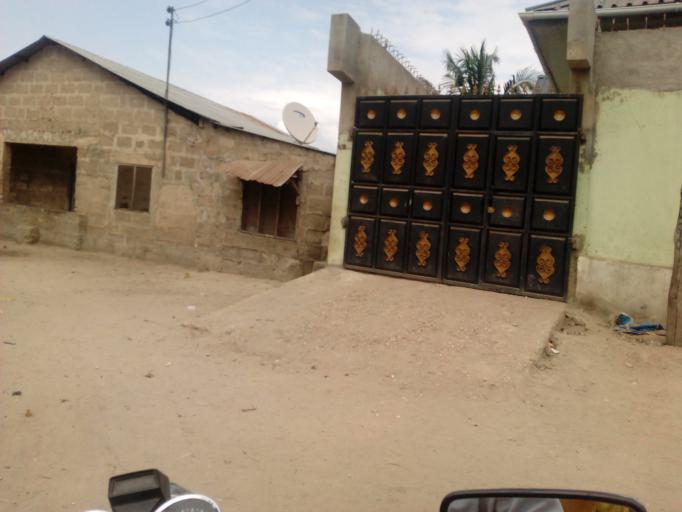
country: TZ
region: Dar es Salaam
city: Dar es Salaam
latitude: -6.8585
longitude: 39.2537
